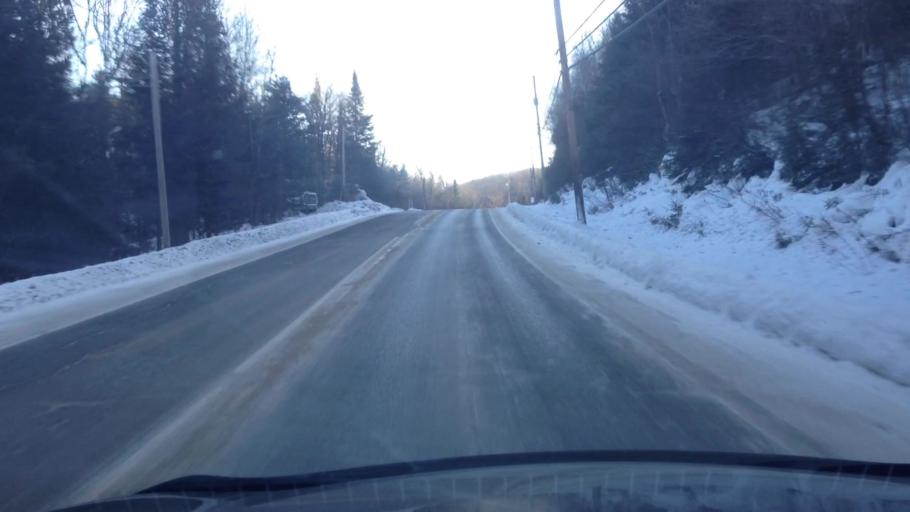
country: CA
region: Quebec
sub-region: Laurentides
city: Sainte-Agathe-des-Monts
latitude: 45.9141
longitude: -74.3610
